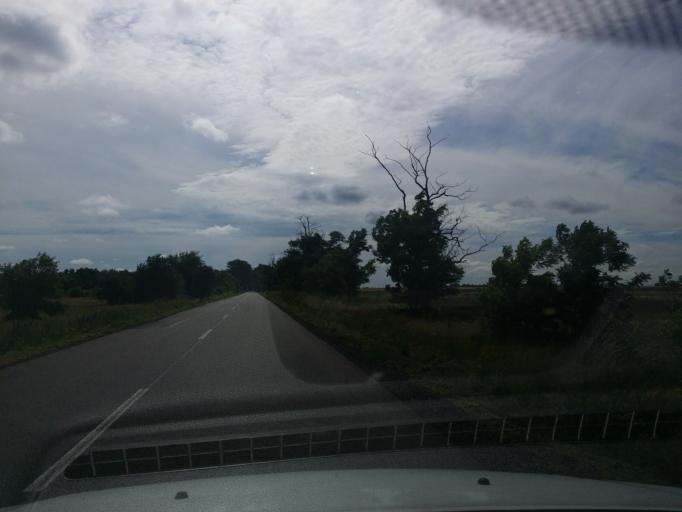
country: HU
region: Heves
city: Besenyotelek
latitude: 47.6054
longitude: 20.4068
